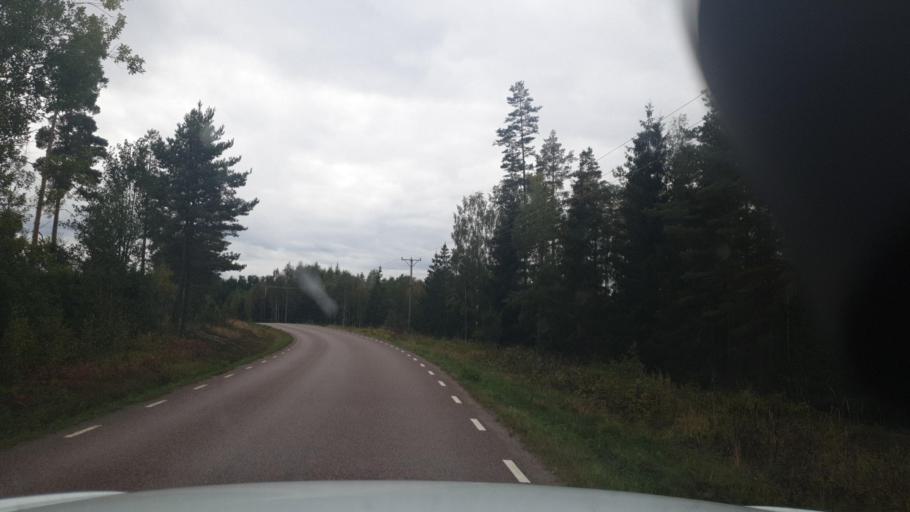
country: SE
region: Vaermland
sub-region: Karlstads Kommun
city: Valberg
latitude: 59.4477
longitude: 13.0917
